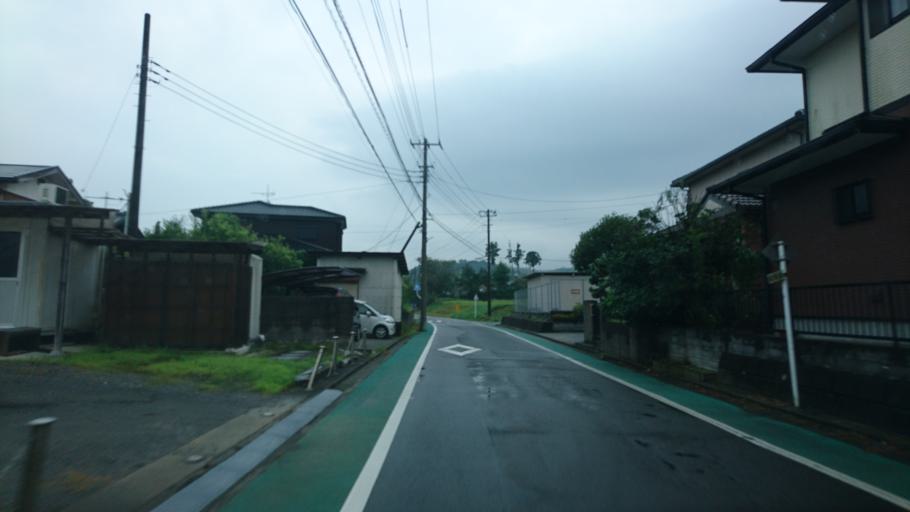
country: JP
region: Chiba
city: Kimitsu
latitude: 35.3038
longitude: 139.9524
